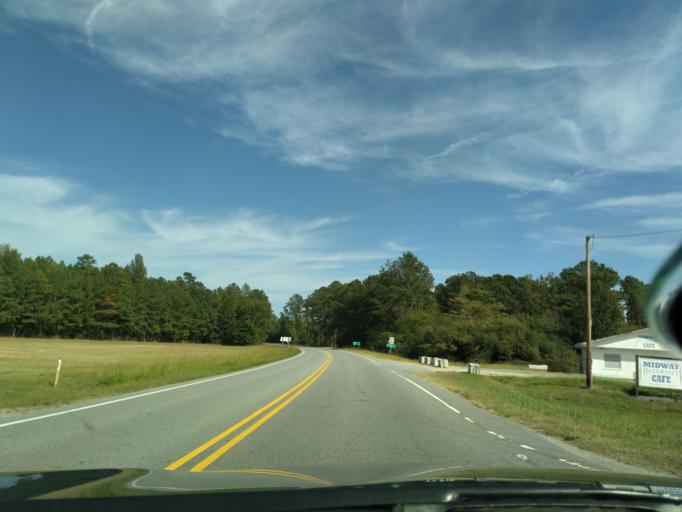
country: US
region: North Carolina
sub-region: Beaufort County
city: River Road
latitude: 35.5122
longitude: -76.9022
